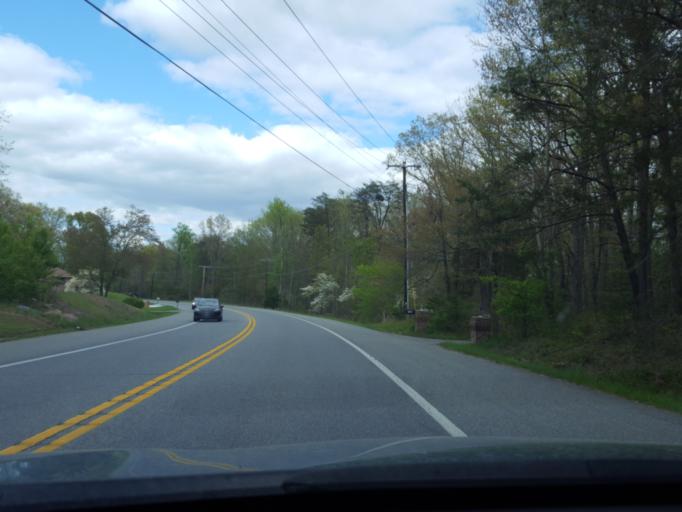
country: US
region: Maryland
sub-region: Charles County
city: Saint Charles
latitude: 38.5449
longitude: -76.9093
